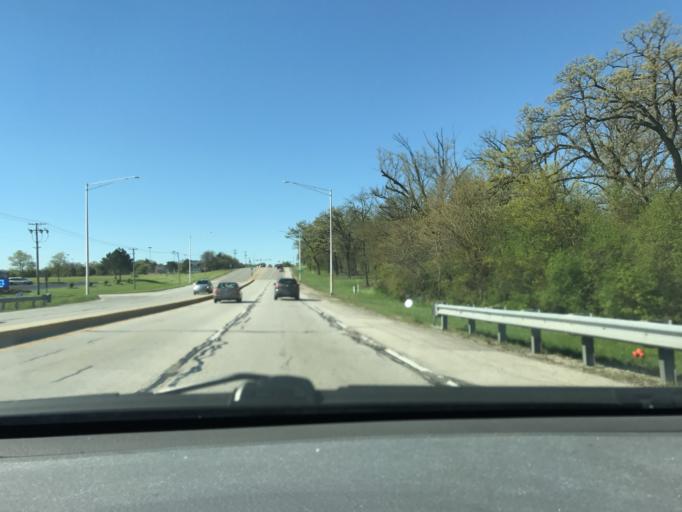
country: US
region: Illinois
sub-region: Kane County
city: Sleepy Hollow
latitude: 42.0566
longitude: -88.3383
